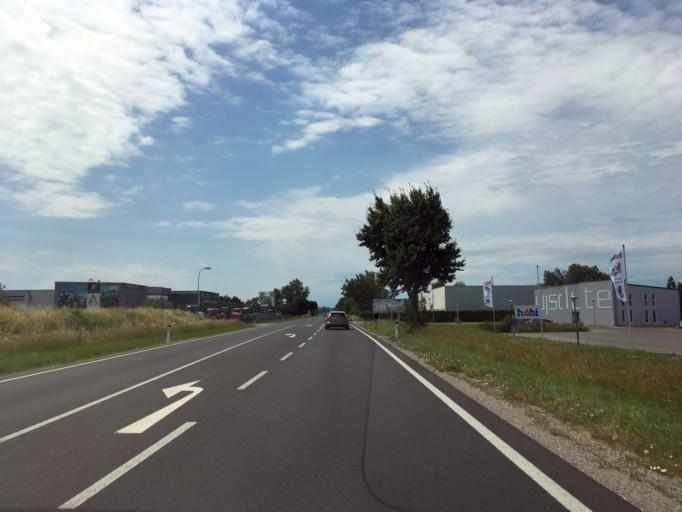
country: AT
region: Lower Austria
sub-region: Politischer Bezirk Baden
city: Teesdorf
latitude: 47.9659
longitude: 16.2748
